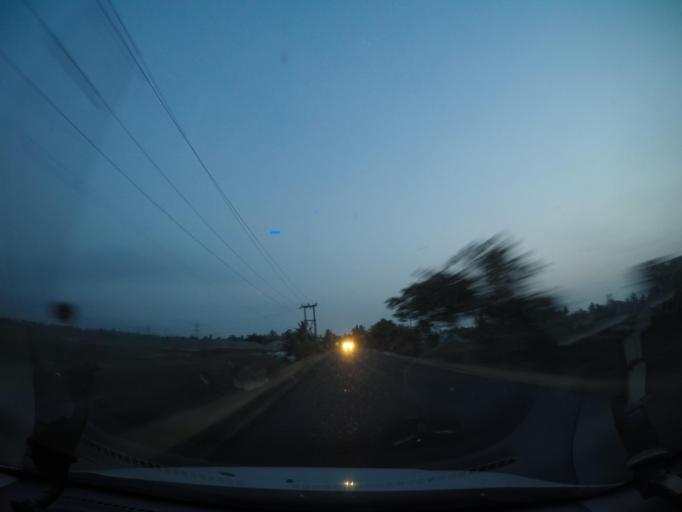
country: IN
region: Andhra Pradesh
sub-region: West Godavari
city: Tadepallegudem
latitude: 16.7778
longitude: 81.4242
